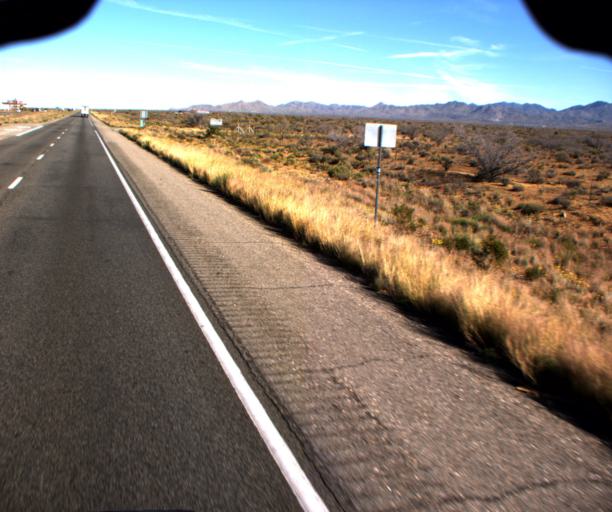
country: US
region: Arizona
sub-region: Mohave County
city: Golden Valley
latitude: 35.3307
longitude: -114.2112
